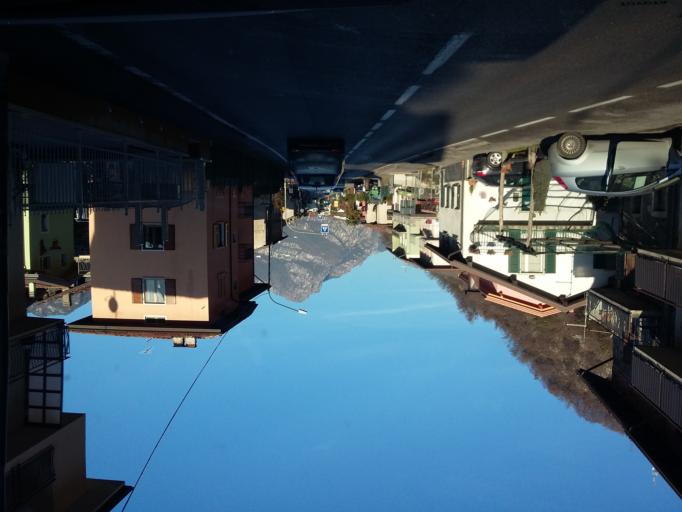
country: IT
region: Lombardy
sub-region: Provincia di Brescia
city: Ponte Caffaro
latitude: 45.8192
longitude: 10.5235
